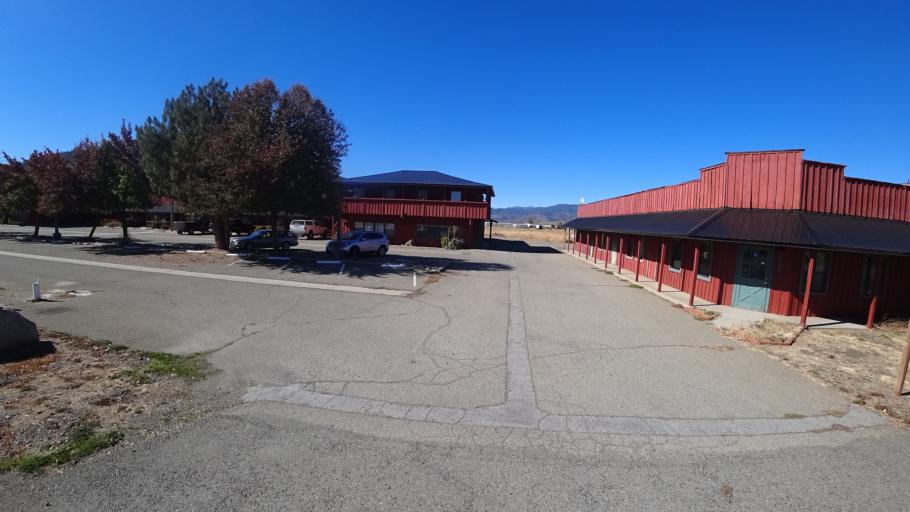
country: US
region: California
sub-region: Siskiyou County
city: Yreka
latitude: 41.6003
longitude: -122.8474
